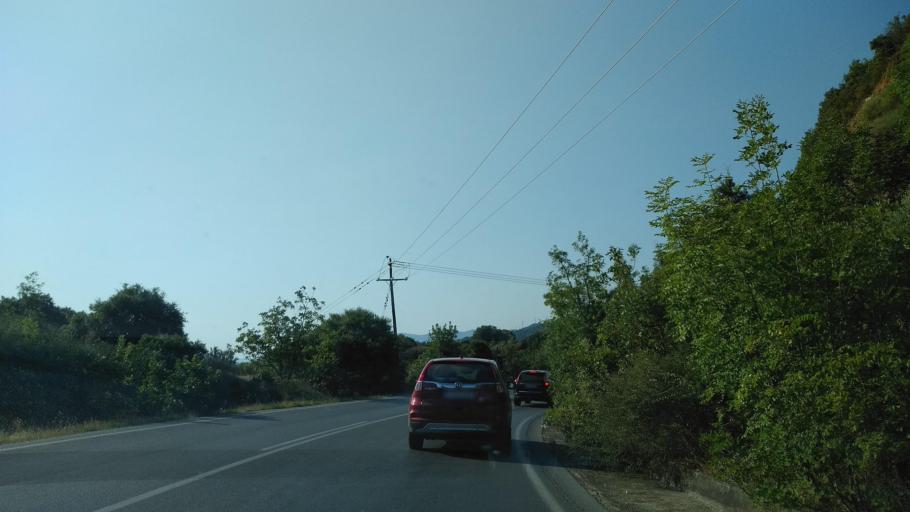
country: GR
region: Central Macedonia
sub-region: Nomos Thessalonikis
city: Stavros
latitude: 40.6498
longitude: 23.7453
